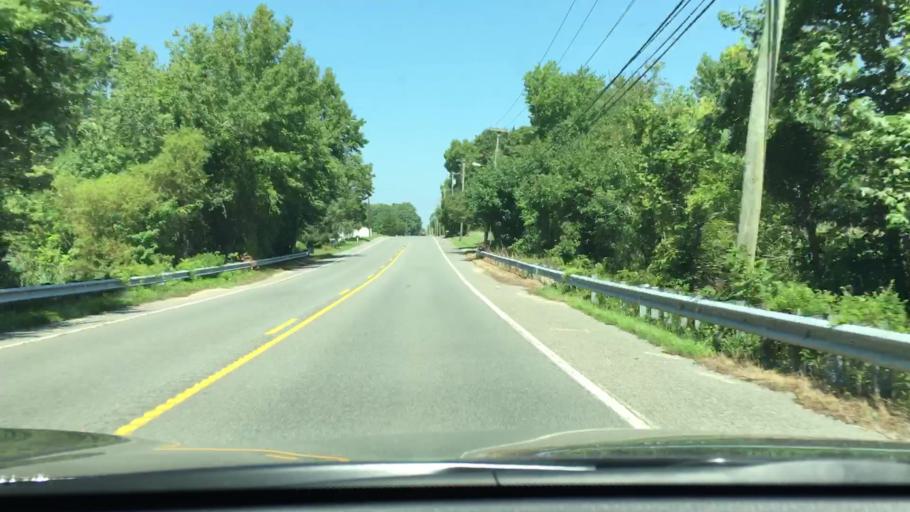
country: US
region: New Jersey
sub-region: Cumberland County
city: Laurel Lake
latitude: 39.3029
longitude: -75.0031
